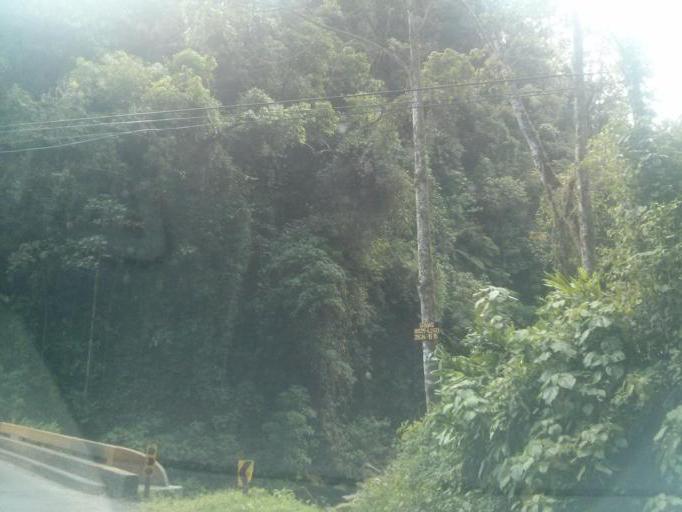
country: CR
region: Cartago
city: Turrialba
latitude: 9.9690
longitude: -83.7386
